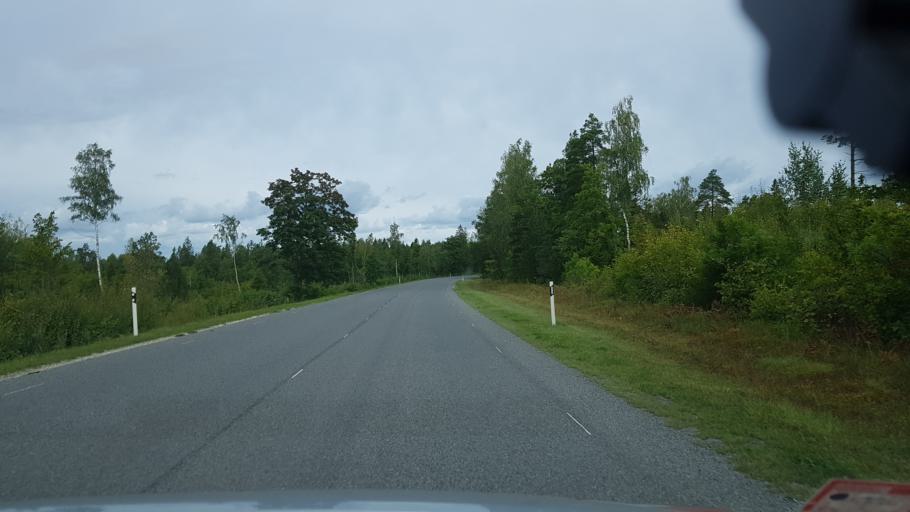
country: EE
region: Saare
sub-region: Kuressaare linn
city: Kuressaare
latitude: 58.4614
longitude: 22.7041
